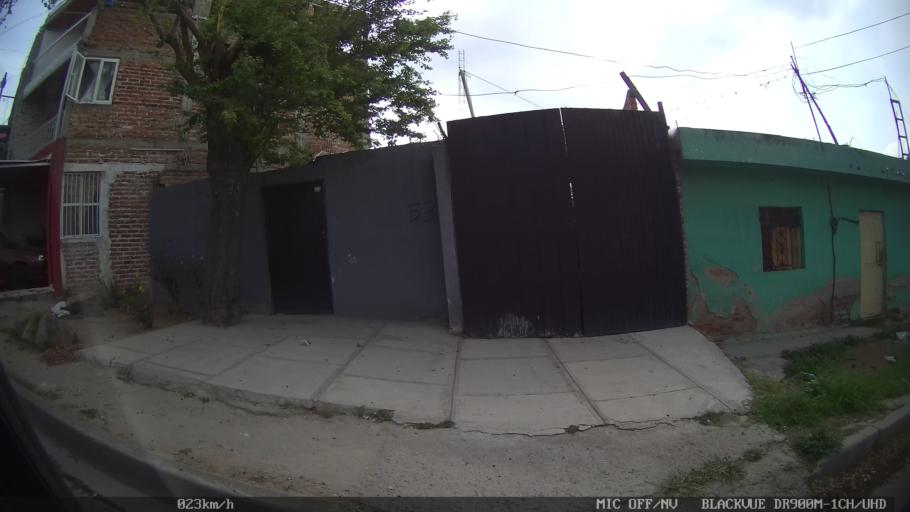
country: MX
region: Jalisco
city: Tonala
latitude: 20.6198
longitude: -103.2321
